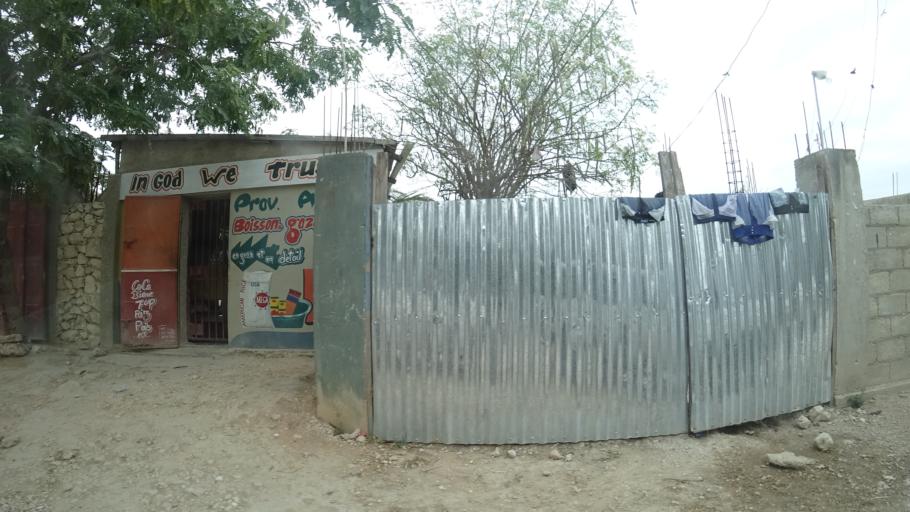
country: HT
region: Ouest
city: Croix des Bouquets
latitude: 18.6548
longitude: -72.2677
